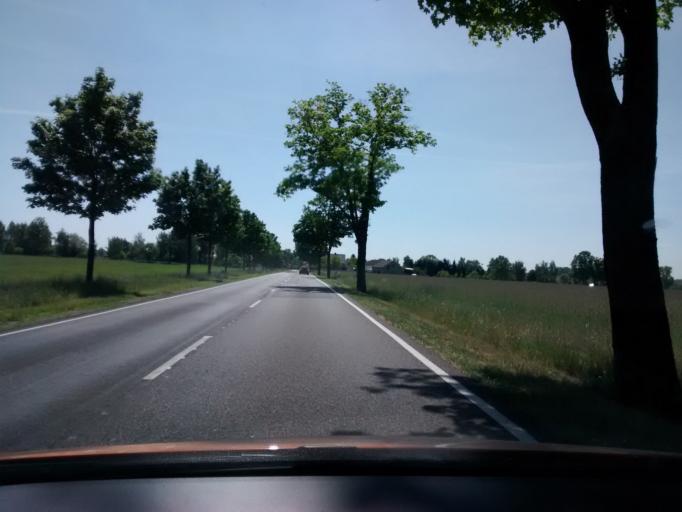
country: DE
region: Brandenburg
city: Storkow
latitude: 52.2891
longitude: 13.9059
